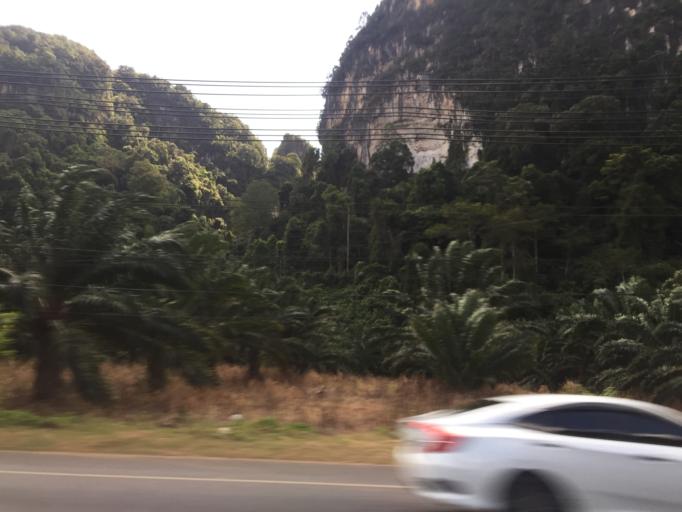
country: TH
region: Phangnga
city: Ban Ao Nang
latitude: 8.0774
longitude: 98.8461
